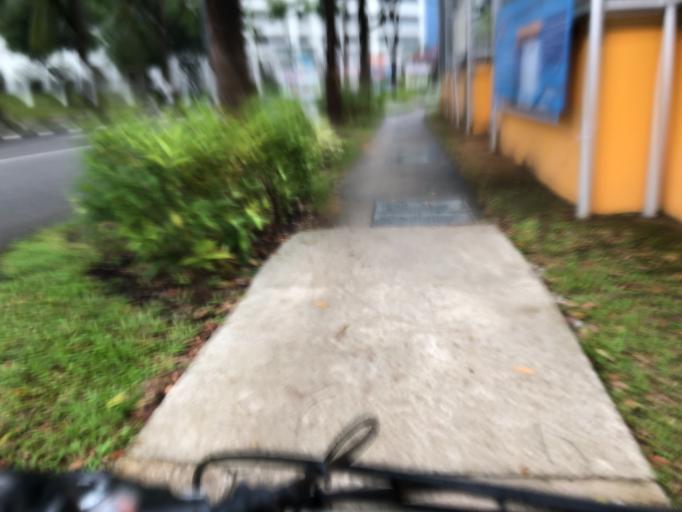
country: MY
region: Johor
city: Johor Bahru
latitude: 1.3593
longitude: 103.7494
